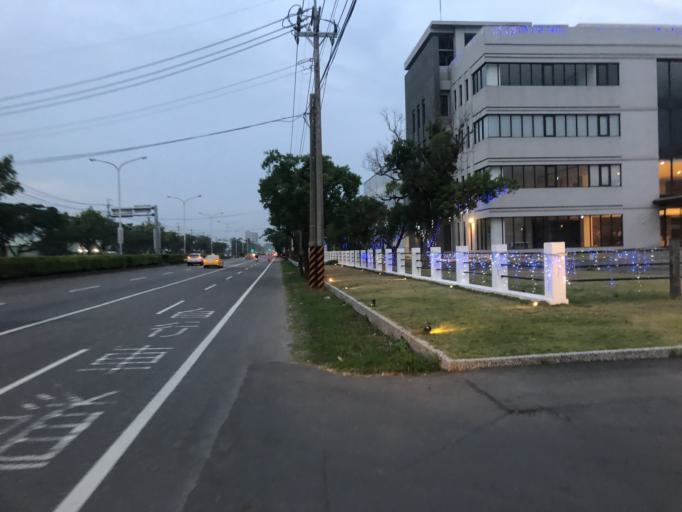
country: TW
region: Taiwan
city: Yujing
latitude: 23.1124
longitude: 120.3185
